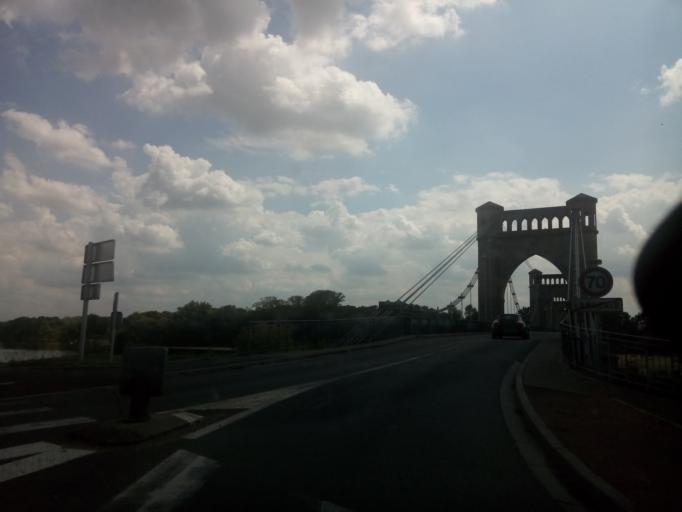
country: FR
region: Centre
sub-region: Departement d'Indre-et-Loire
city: Langeais
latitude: 47.3211
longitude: 0.4028
